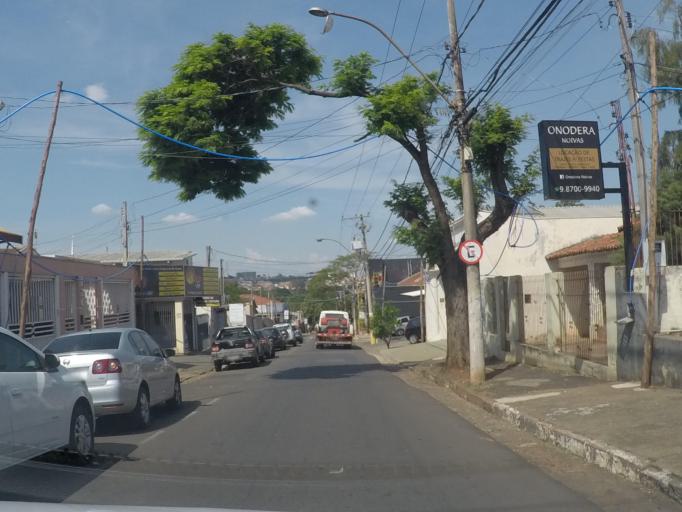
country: BR
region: Sao Paulo
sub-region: Sumare
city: Sumare
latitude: -22.8237
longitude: -47.2648
